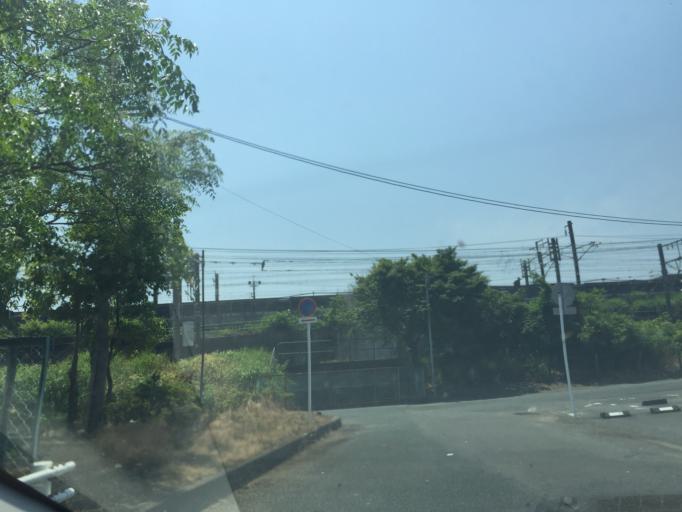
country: JP
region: Shizuoka
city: Kakegawa
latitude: 34.7691
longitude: 138.0086
